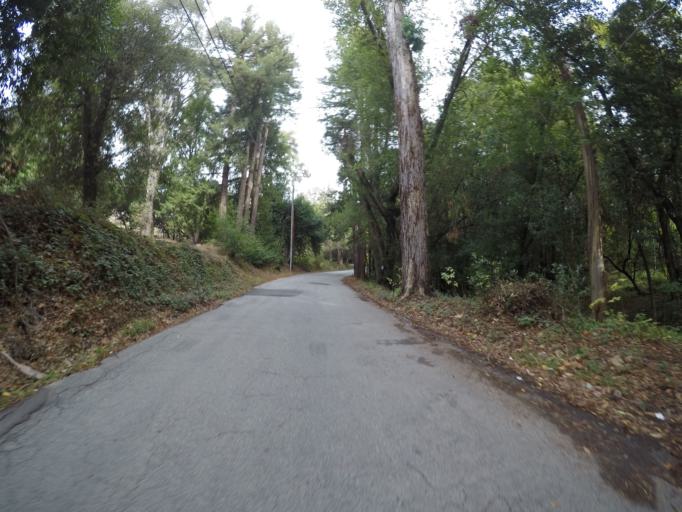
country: US
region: California
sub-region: Santa Cruz County
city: Scotts Valley
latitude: 37.0295
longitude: -121.9849
